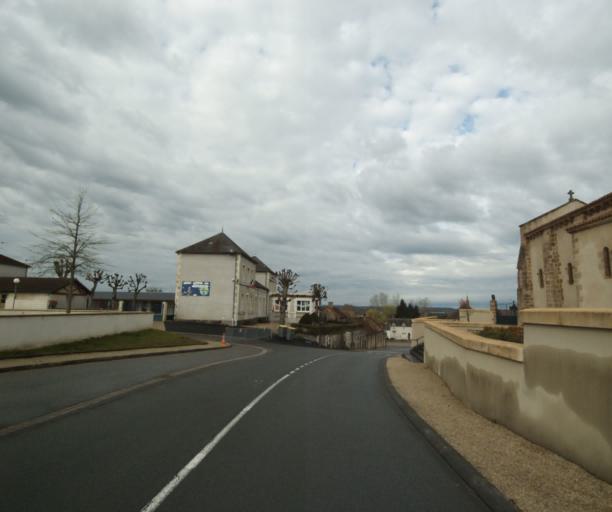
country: FR
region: Auvergne
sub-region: Departement de l'Allier
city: Toulon-sur-Allier
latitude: 46.5184
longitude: 3.3595
